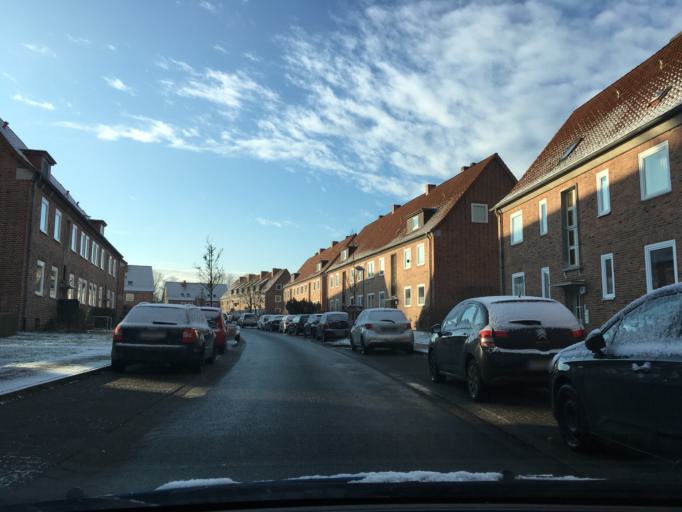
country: DE
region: Lower Saxony
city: Lueneburg
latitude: 53.2341
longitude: 10.3981
